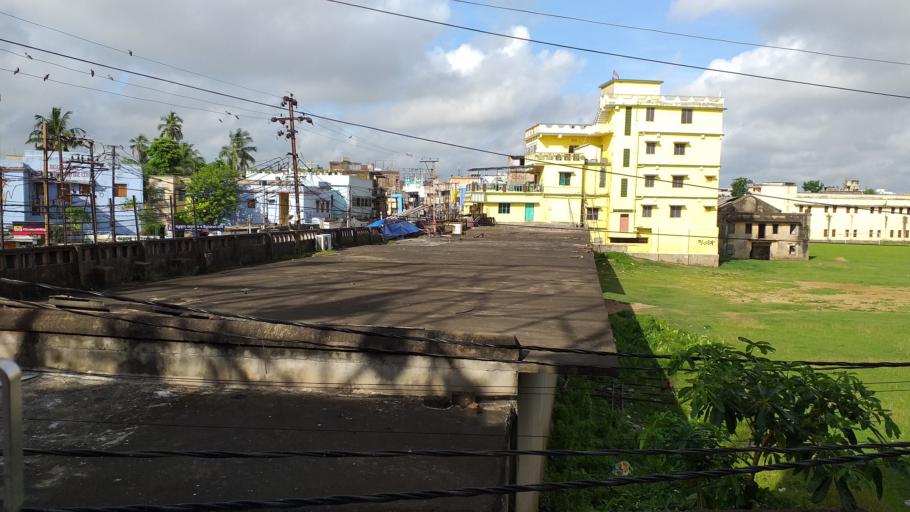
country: IN
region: Odisha
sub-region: Cuttack
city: Cuttack
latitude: 20.4707
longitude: 85.8715
